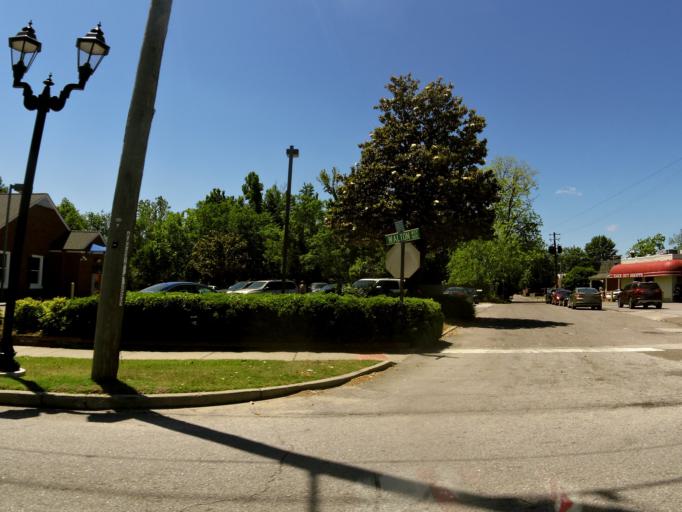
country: US
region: Georgia
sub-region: Richmond County
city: Augusta
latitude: 33.4754
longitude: -81.9929
